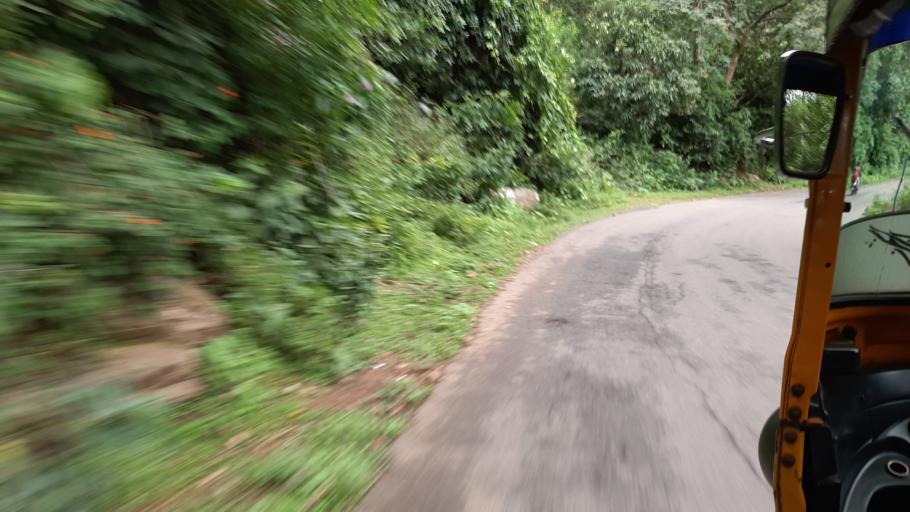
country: IN
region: Andhra Pradesh
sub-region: Vizianagaram District
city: Salur
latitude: 18.2434
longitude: 83.0187
